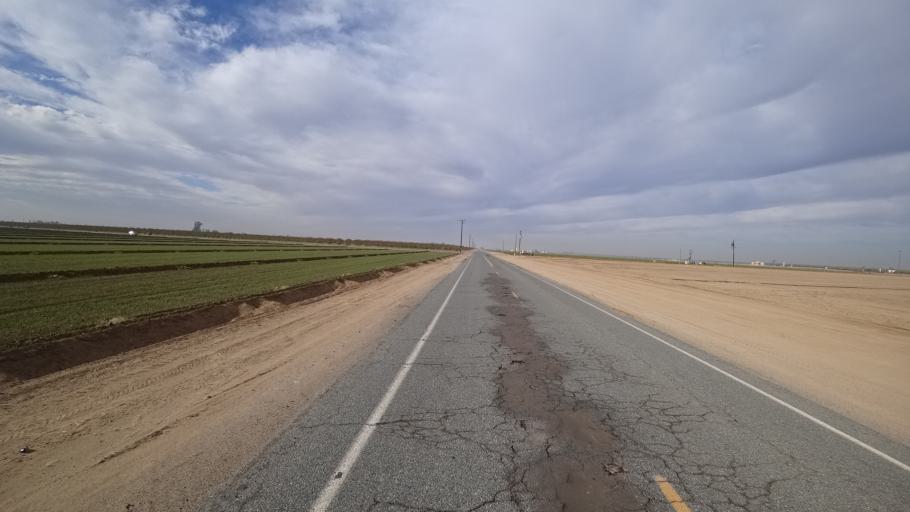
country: US
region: California
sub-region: Kern County
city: Rosedale
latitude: 35.4124
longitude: -119.1705
